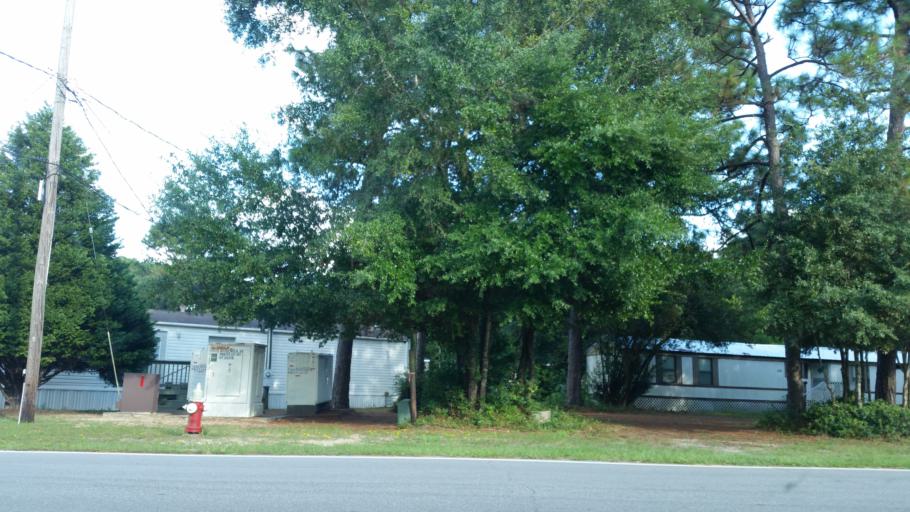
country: US
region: Florida
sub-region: Escambia County
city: Ferry Pass
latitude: 30.5009
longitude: -87.1757
